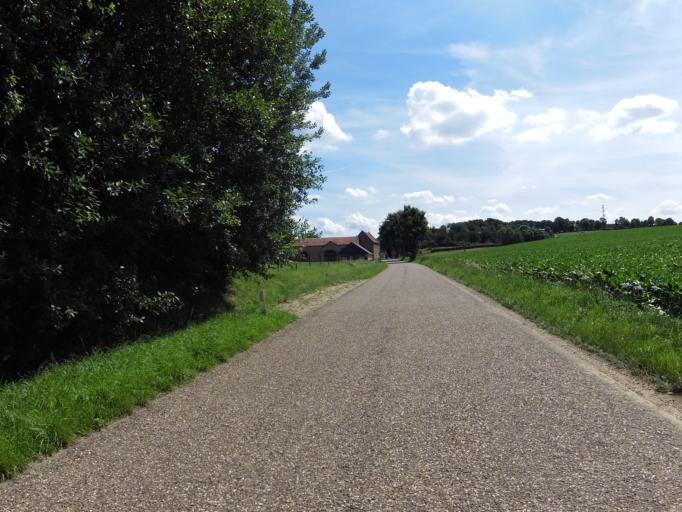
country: NL
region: Limburg
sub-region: Gemeente Voerendaal
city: Kunrade
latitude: 50.8659
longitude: 5.9300
